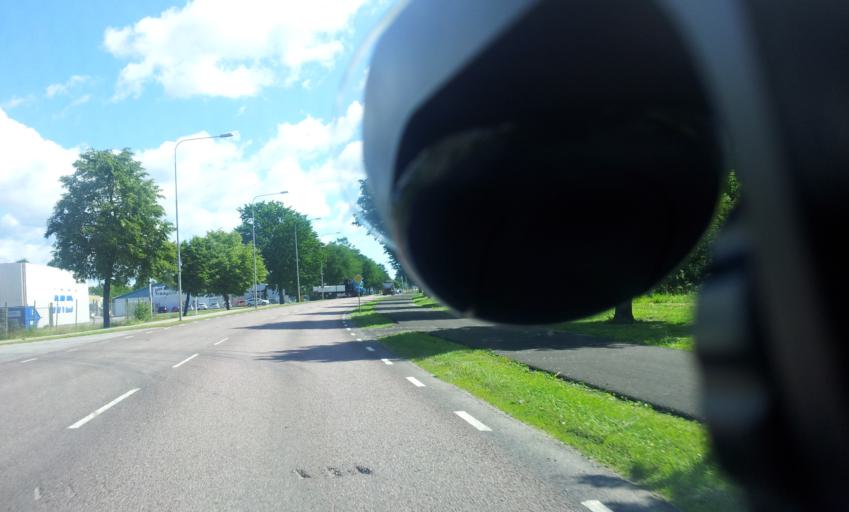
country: SE
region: Kalmar
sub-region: Oskarshamns Kommun
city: Oskarshamn
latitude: 57.2496
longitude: 16.4369
